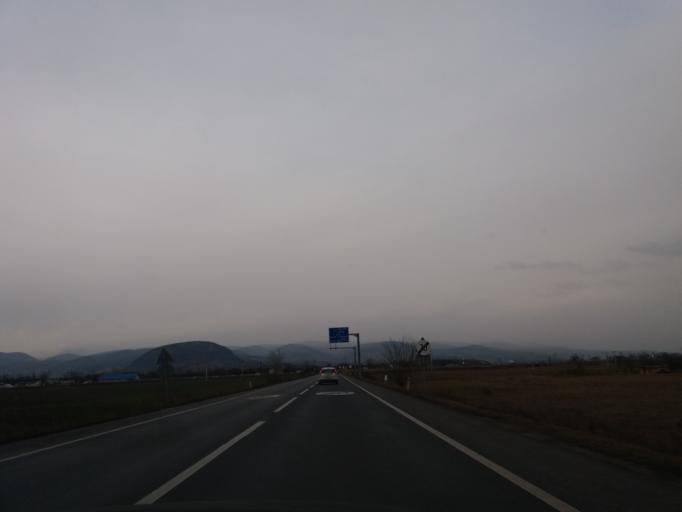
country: RO
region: Hunedoara
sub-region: Oras Simeria
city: Simeria
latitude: 45.8311
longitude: 23.0372
